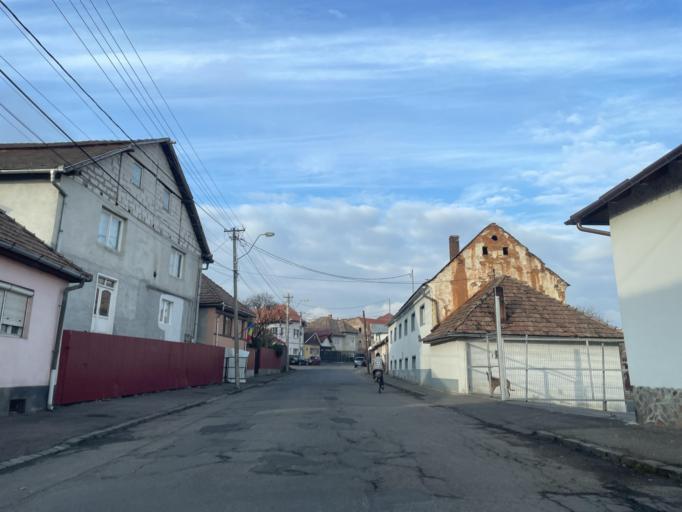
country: RO
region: Mures
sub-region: Municipiul Reghin
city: Reghin
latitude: 46.7722
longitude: 24.6975
